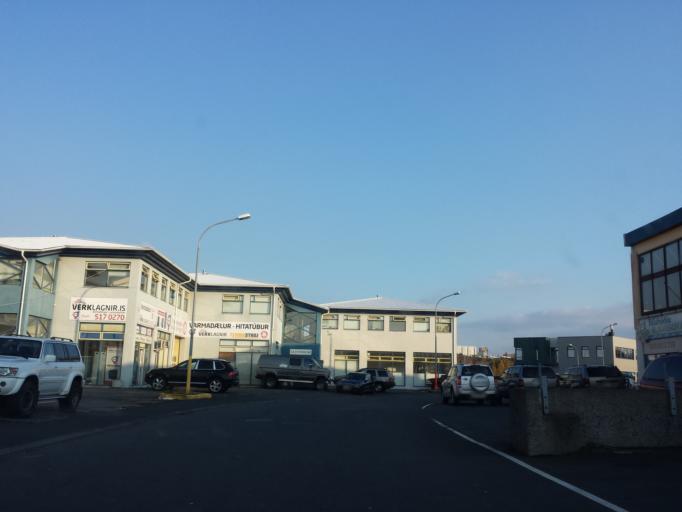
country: IS
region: Capital Region
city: Reykjavik
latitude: 64.1128
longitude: -21.8482
